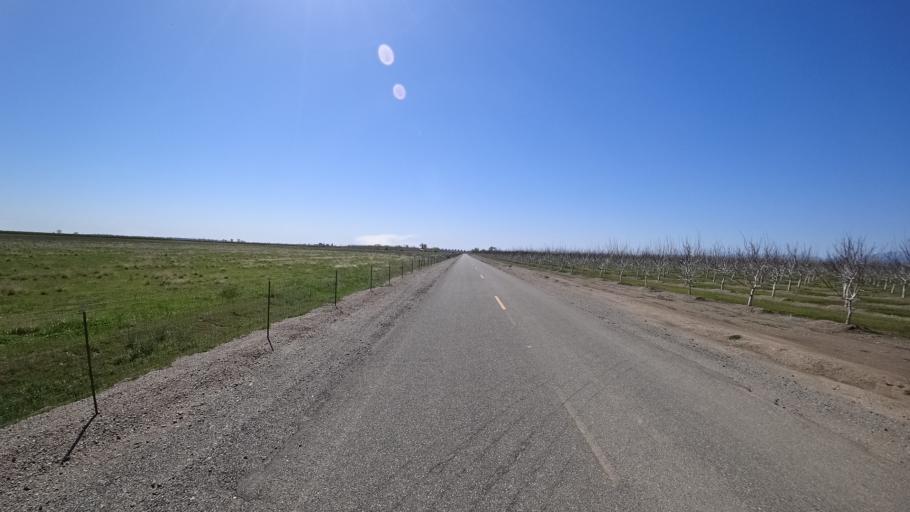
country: US
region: California
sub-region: Glenn County
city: Willows
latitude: 39.6317
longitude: -122.2535
